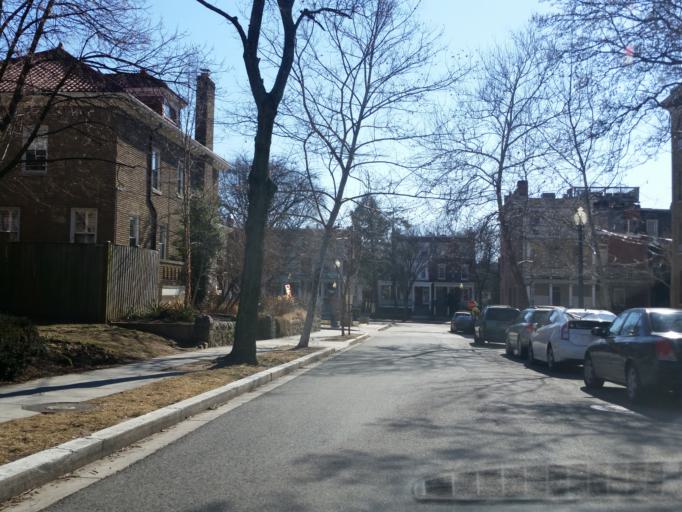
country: US
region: Washington, D.C.
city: Washington, D.C.
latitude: 38.9333
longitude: -77.0399
